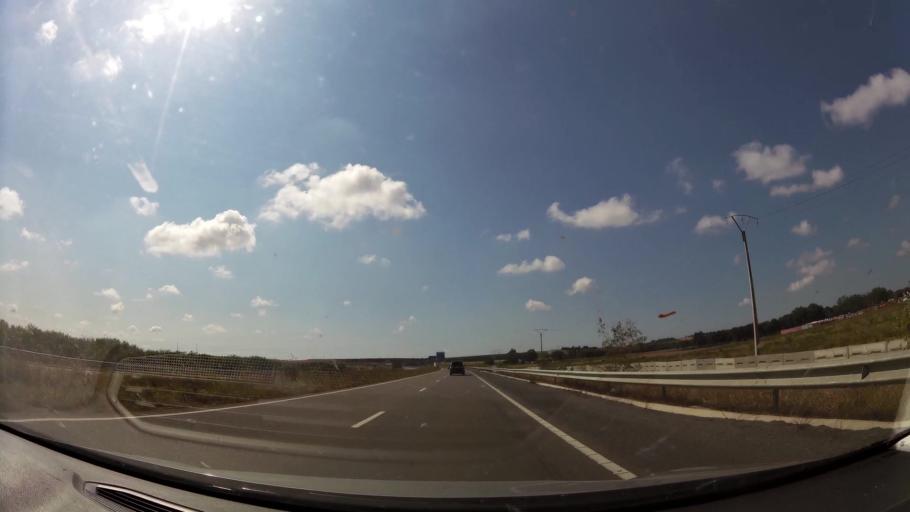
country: MA
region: Rabat-Sale-Zemmour-Zaer
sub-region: Skhirate-Temara
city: Temara
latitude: 33.8419
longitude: -6.8868
